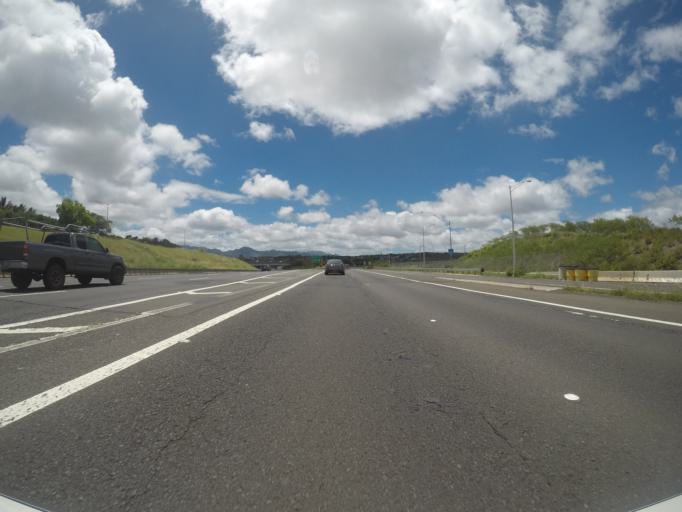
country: US
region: Hawaii
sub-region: Honolulu County
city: Pearl City, Manana
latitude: 21.3966
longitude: -157.9850
